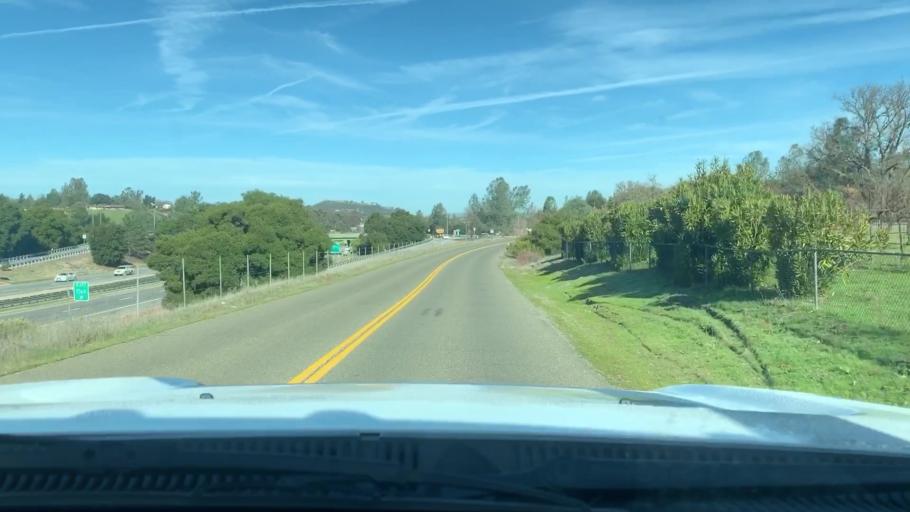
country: US
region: California
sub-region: San Luis Obispo County
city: Santa Margarita
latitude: 35.4412
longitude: -120.6374
